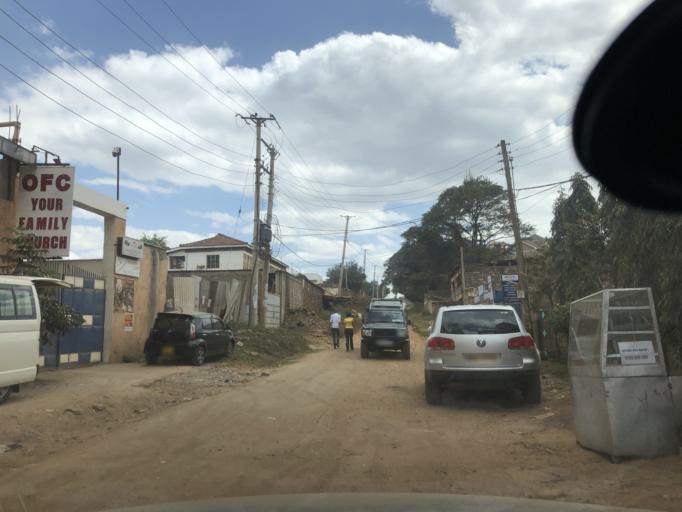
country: KE
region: Nairobi Area
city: Pumwani
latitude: -1.2287
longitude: 36.8789
